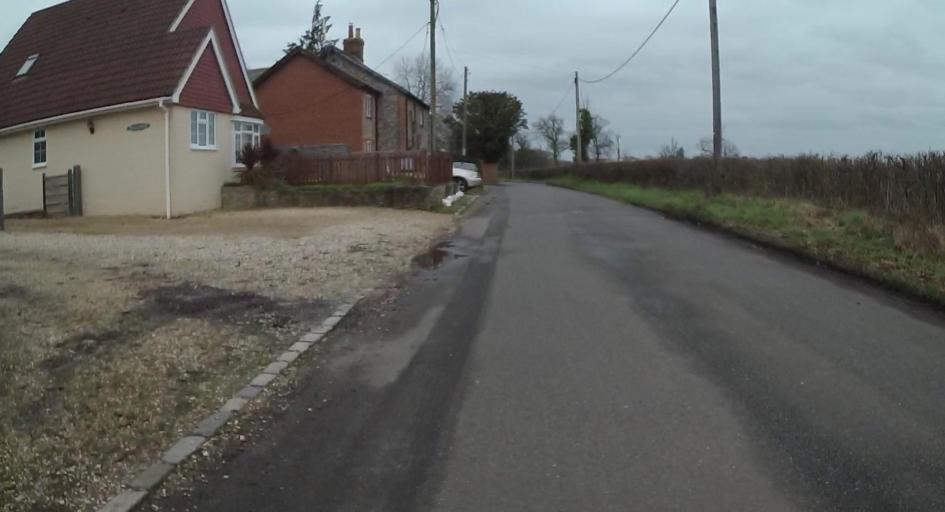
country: GB
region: England
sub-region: West Berkshire
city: Stratfield Mortimer
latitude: 51.3778
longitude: -1.0388
